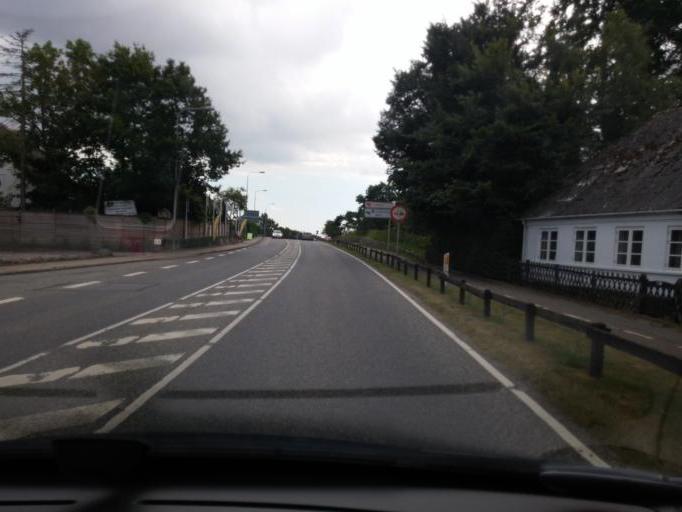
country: DK
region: South Denmark
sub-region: Svendborg Kommune
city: Vindeby
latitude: 55.0212
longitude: 10.6076
